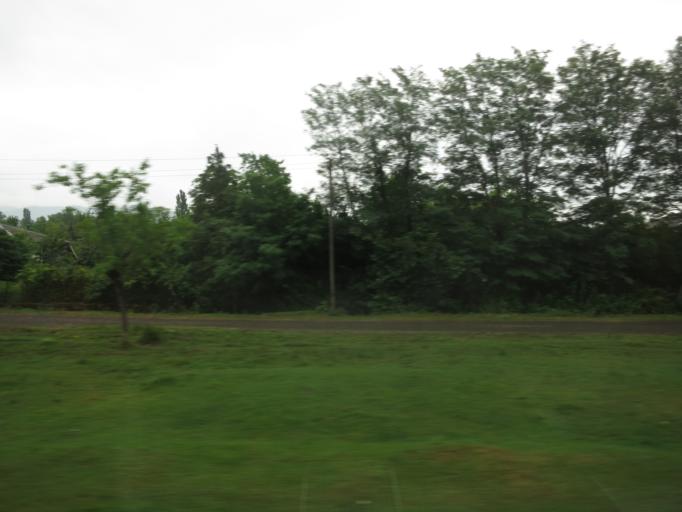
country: GE
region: Guria
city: Lanchkhuti
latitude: 42.0879
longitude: 41.9605
